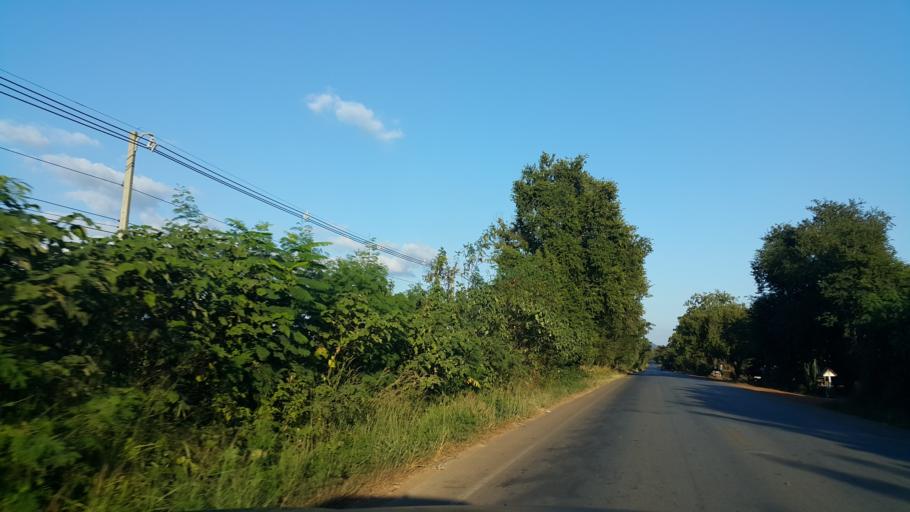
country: TH
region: Sukhothai
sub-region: Amphoe Si Satchanalai
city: Si Satchanalai
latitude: 17.5442
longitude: 99.8329
